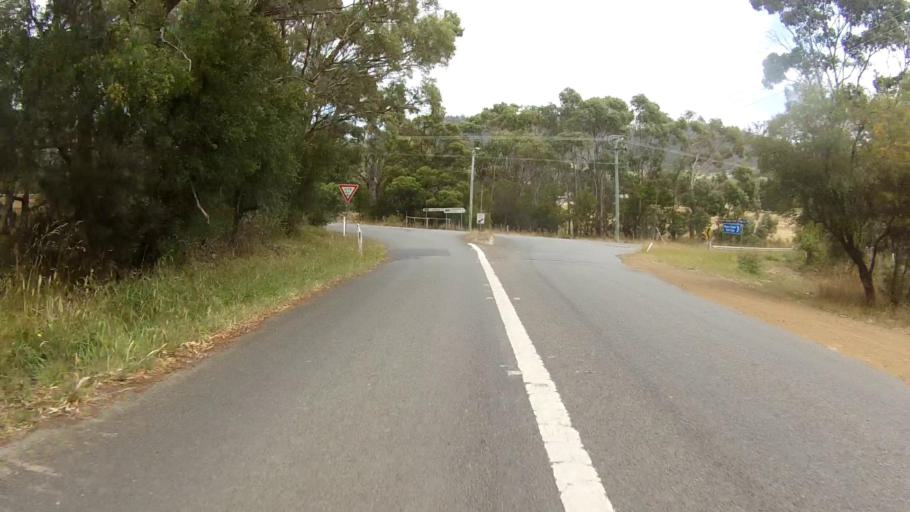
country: AU
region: Tasmania
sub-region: Clarence
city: Acton Park
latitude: -42.8680
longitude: 147.4847
